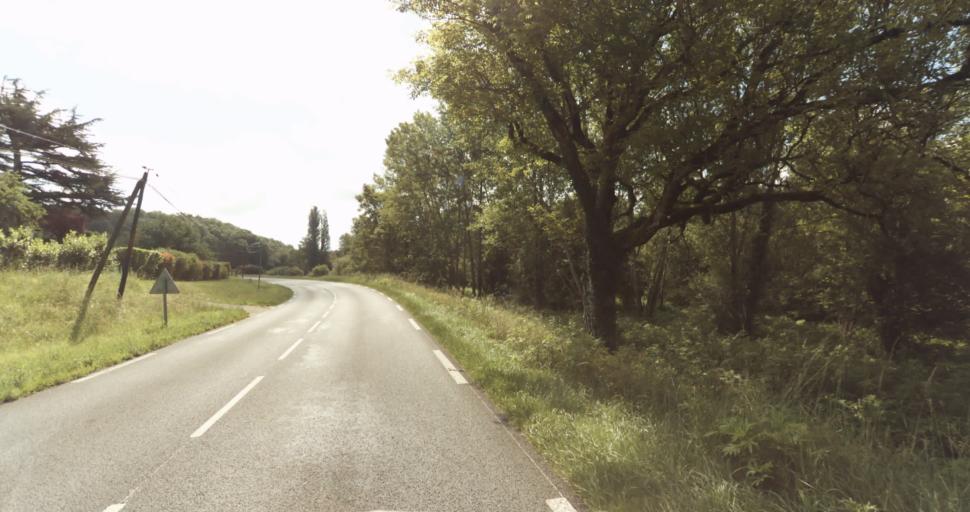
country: FR
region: Aquitaine
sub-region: Departement de la Dordogne
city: Le Bugue
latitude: 44.8412
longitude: 0.8538
